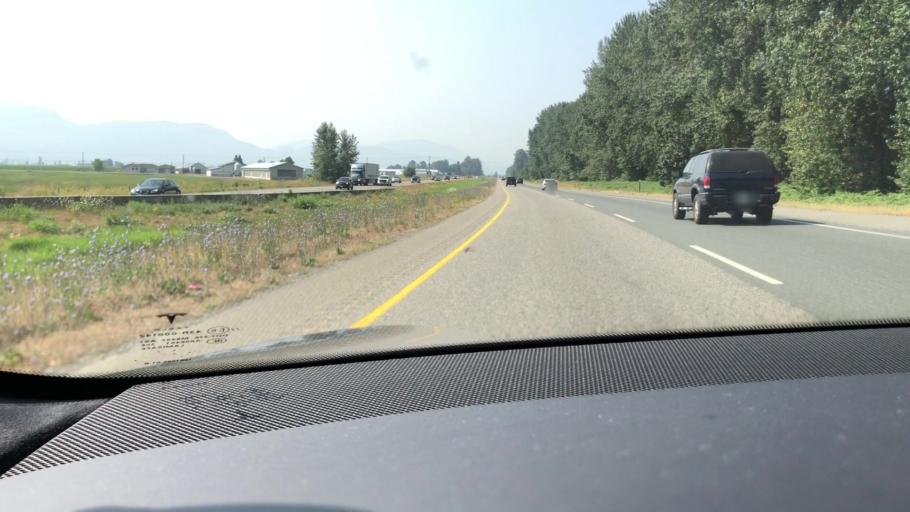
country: CA
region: British Columbia
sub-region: Fraser Valley Regional District
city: Chilliwack
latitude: 49.1206
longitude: -122.1016
